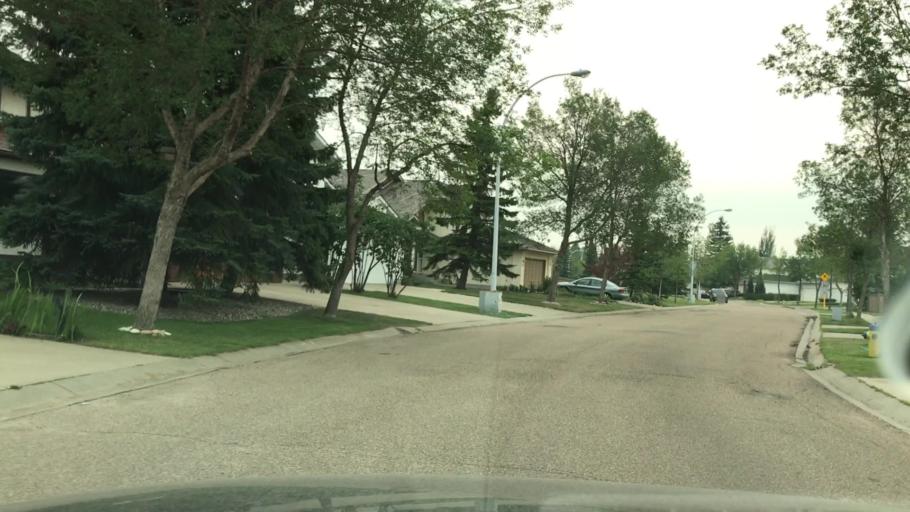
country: CA
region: Alberta
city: Edmonton
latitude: 53.4718
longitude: -113.5752
